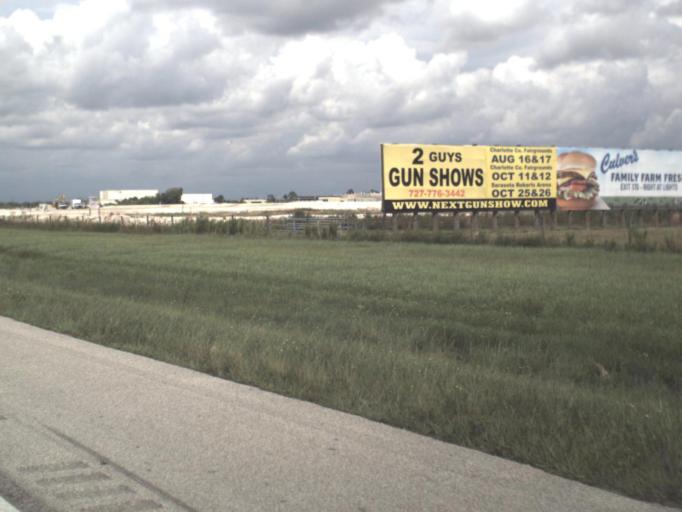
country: US
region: Florida
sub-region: Charlotte County
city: Punta Gorda
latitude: 26.9092
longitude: -82.0098
